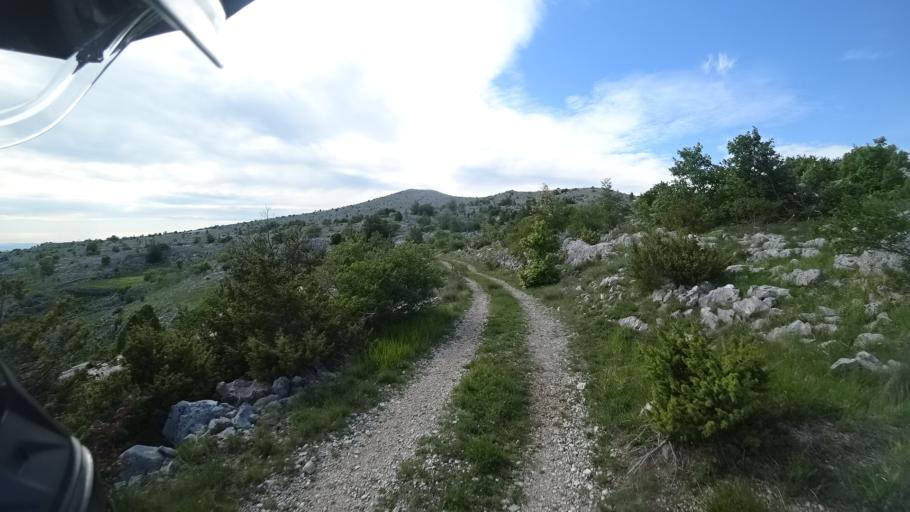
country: HR
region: Splitsko-Dalmatinska
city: Hrvace
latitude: 43.8009
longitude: 16.4323
